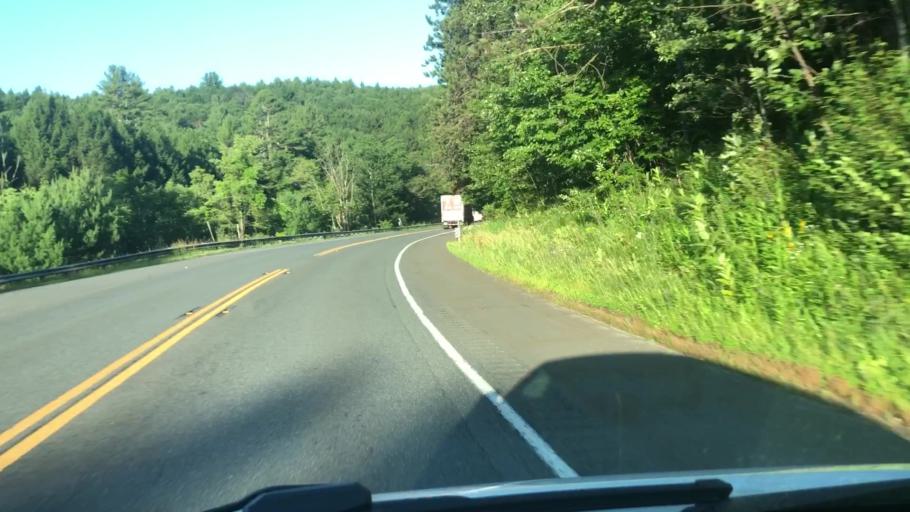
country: US
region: Massachusetts
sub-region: Hampshire County
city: Chesterfield
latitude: 42.4412
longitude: -72.8622
